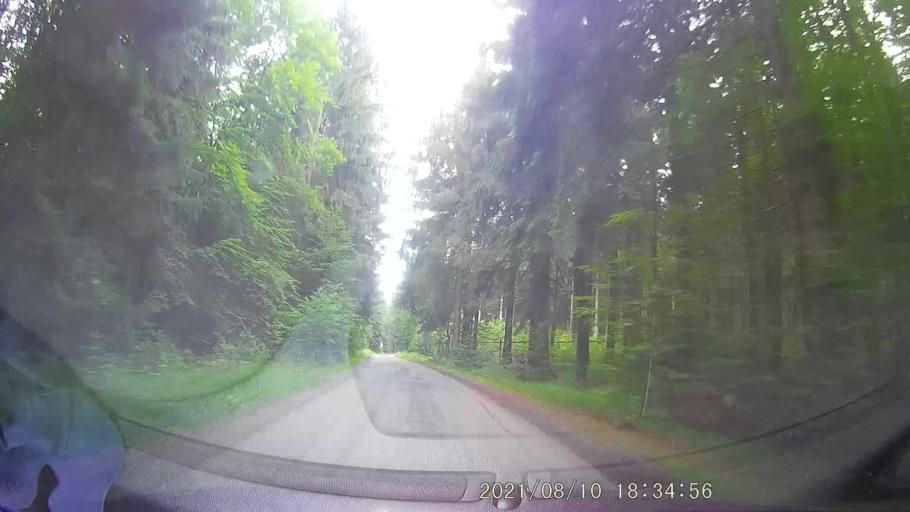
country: PL
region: Lower Silesian Voivodeship
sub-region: Powiat klodzki
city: Radkow
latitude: 50.4801
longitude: 16.3537
